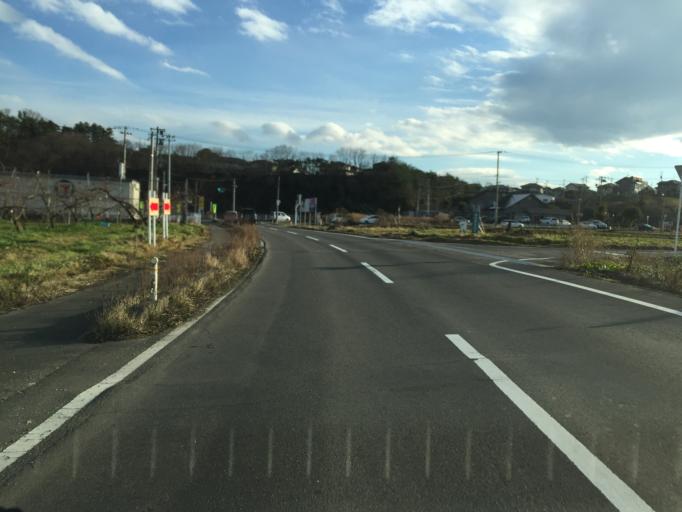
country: JP
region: Fukushima
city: Fukushima-shi
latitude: 37.7270
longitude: 140.4059
